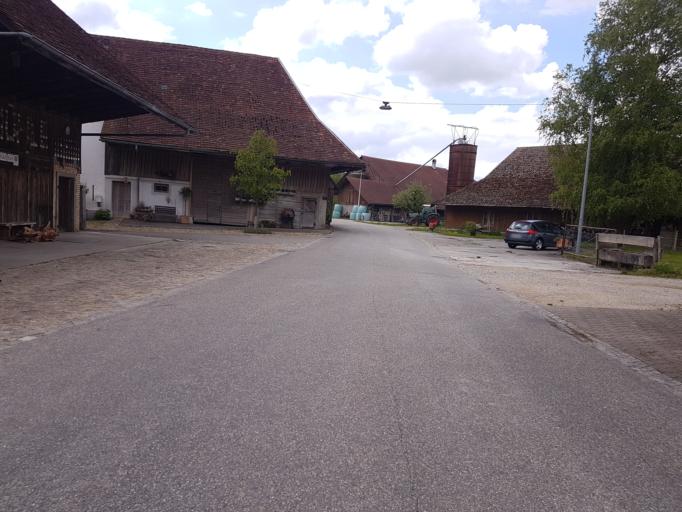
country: CH
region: Solothurn
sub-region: Bezirk Gaeu
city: Wolfwil
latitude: 47.2676
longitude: 7.7977
